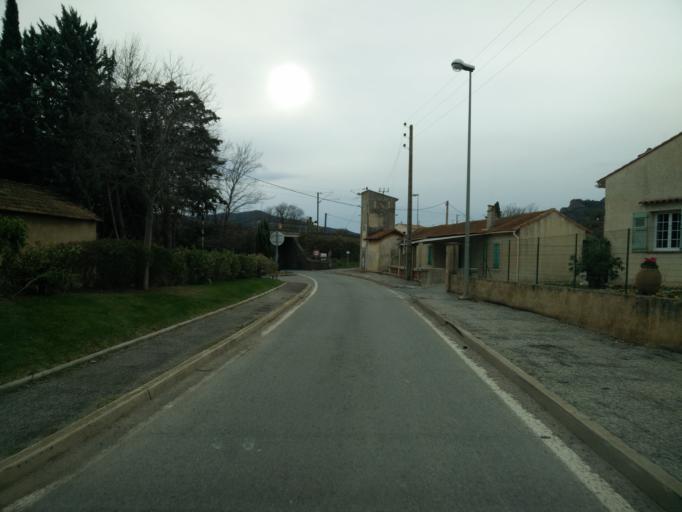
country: FR
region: Provence-Alpes-Cote d'Azur
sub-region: Departement du Var
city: Roquebrune-sur-Argens
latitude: 43.4575
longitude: 6.6343
